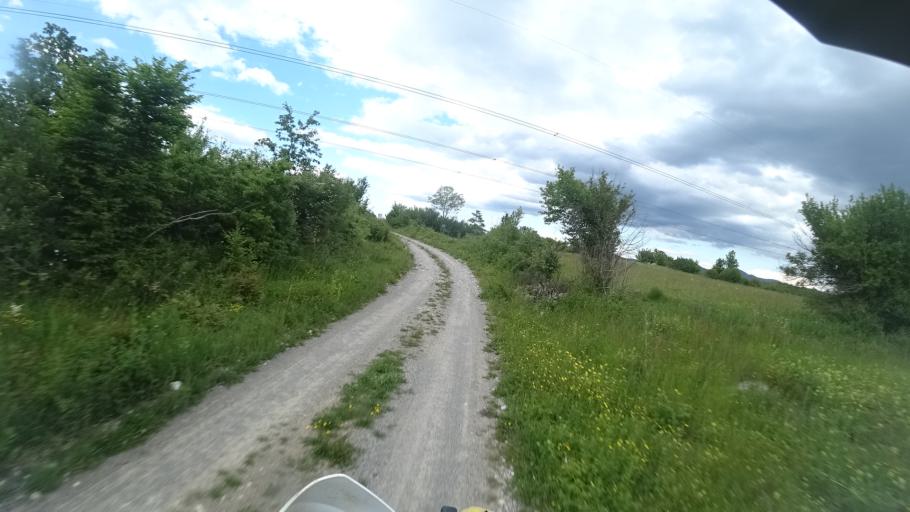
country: HR
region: Zadarska
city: Obrovac
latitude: 44.3516
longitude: 15.6545
